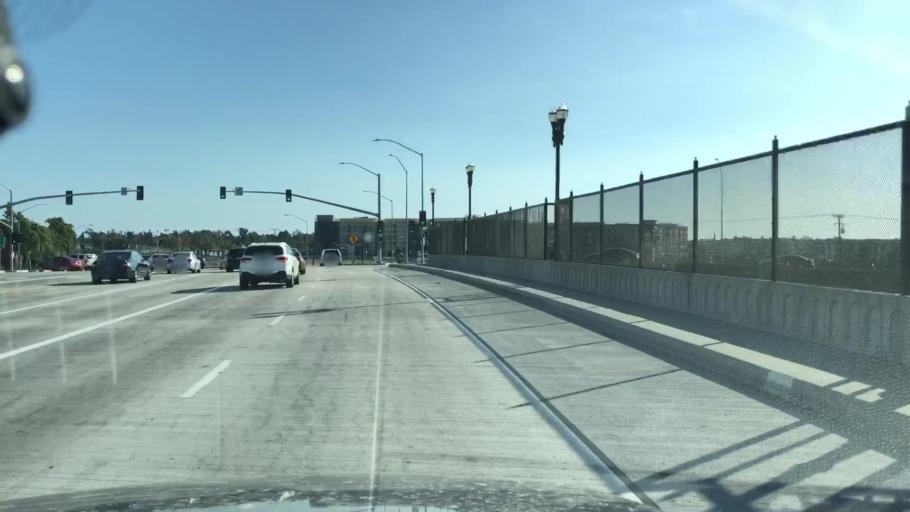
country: US
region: California
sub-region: Ventura County
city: El Rio
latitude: 34.2396
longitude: -119.1811
